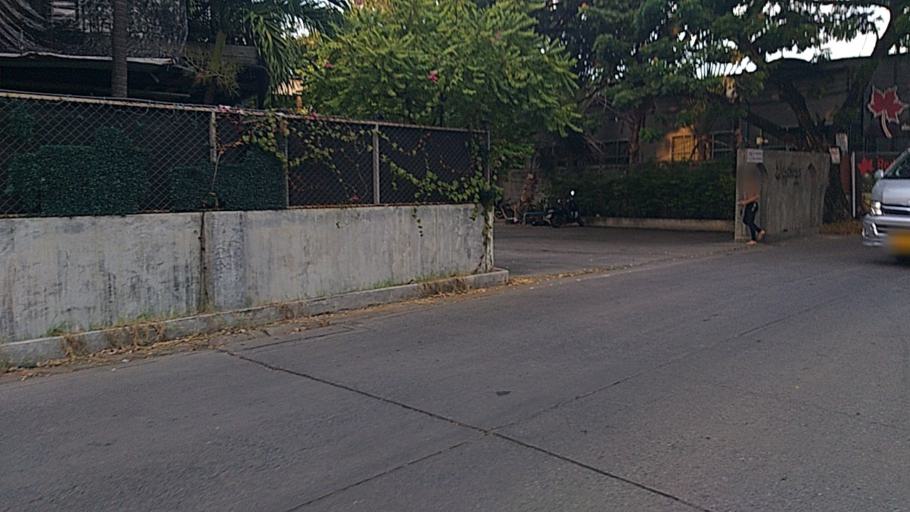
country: TH
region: Bangkok
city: Lat Phrao
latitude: 13.8320
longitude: 100.6209
